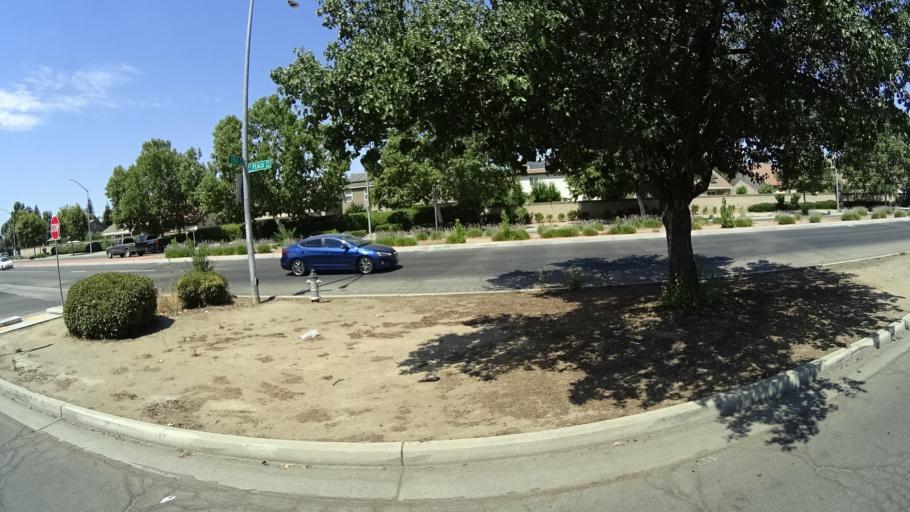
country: US
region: California
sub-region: Fresno County
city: Sunnyside
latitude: 36.7298
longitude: -119.7181
